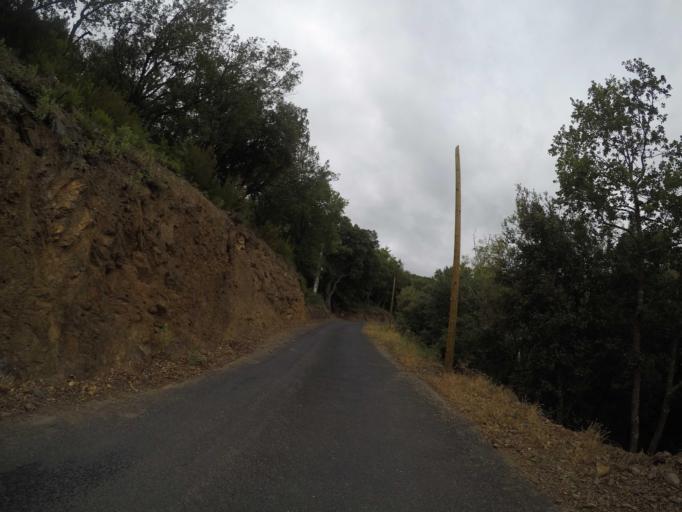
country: FR
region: Languedoc-Roussillon
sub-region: Departement des Pyrenees-Orientales
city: Ille-sur-Tet
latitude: 42.6369
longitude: 2.6212
